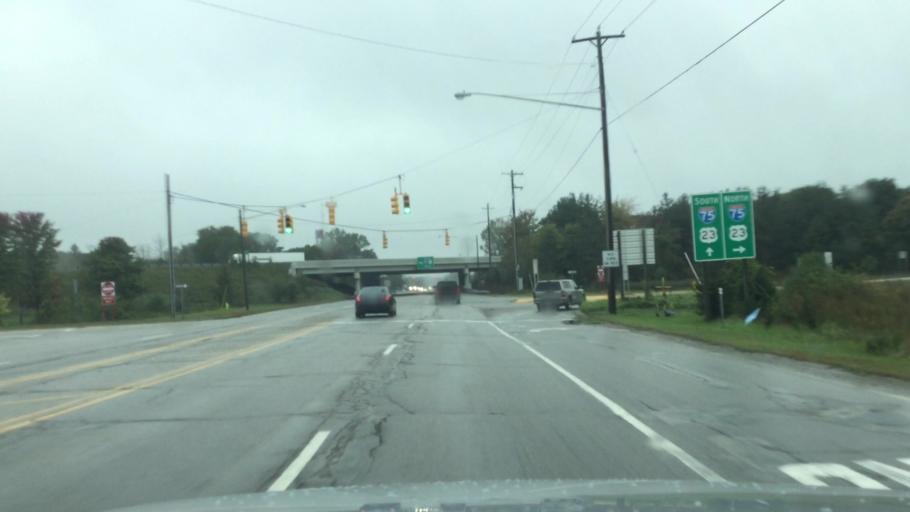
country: US
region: Michigan
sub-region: Saginaw County
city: Bridgeport
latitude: 43.3496
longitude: -83.8622
